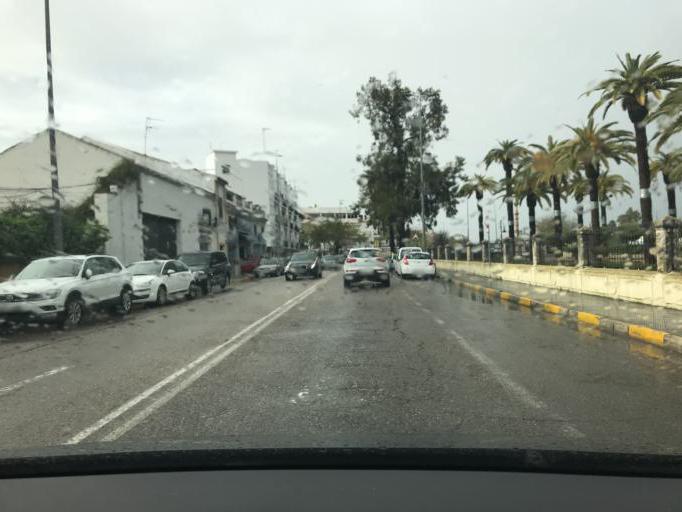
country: ES
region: Andalusia
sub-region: Provincia de Sevilla
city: Ecija
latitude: 37.5422
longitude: -5.0732
